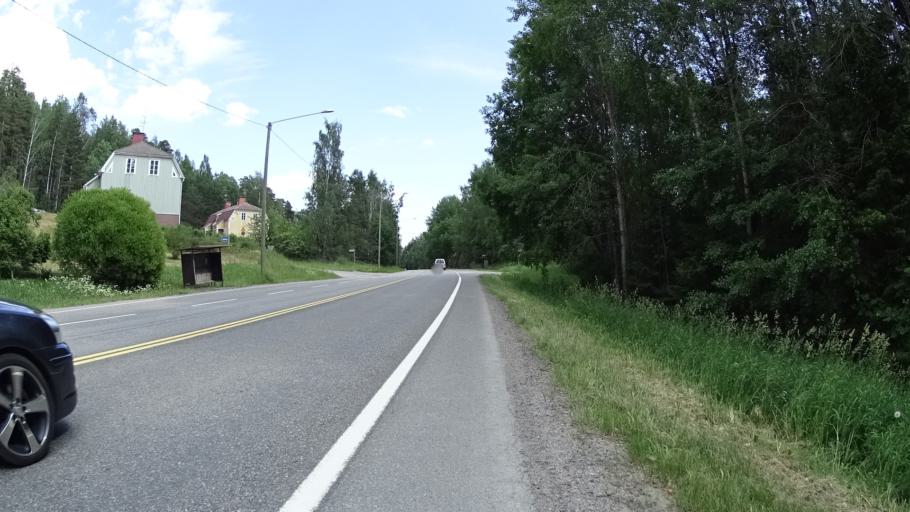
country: FI
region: Uusimaa
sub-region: Raaseporin
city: Pohja
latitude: 60.0992
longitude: 23.5839
